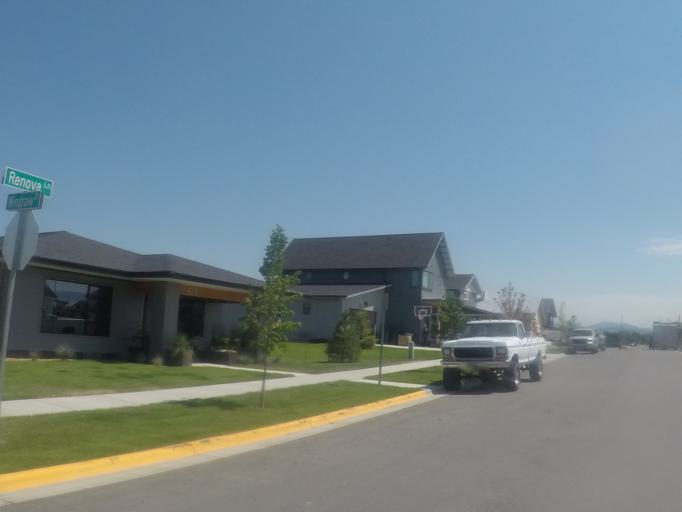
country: US
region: Montana
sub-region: Gallatin County
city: Bozeman
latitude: 45.6906
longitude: -111.0959
